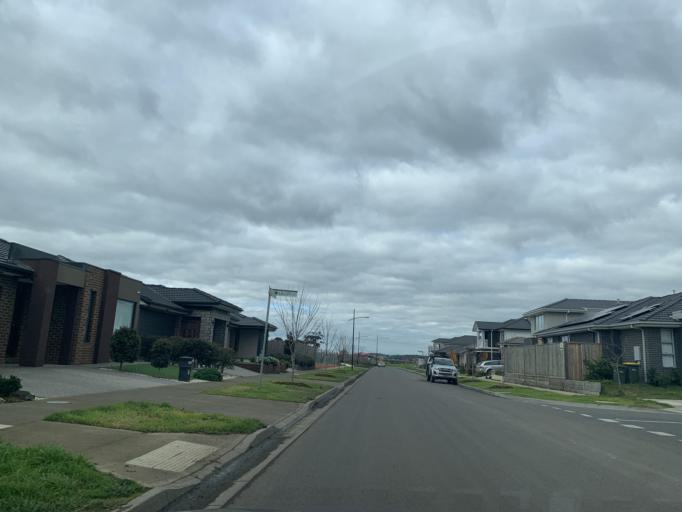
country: AU
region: Victoria
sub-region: Hume
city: Craigieburn
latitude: -37.6028
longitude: 144.9969
